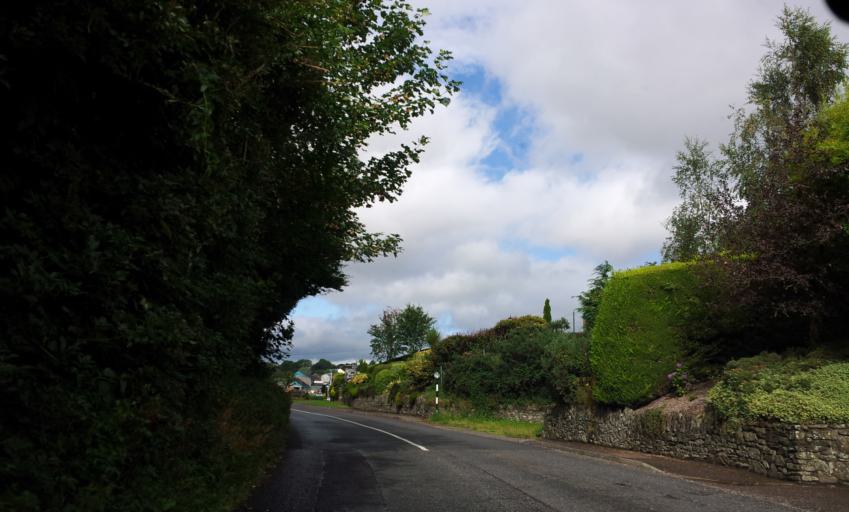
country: IE
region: Munster
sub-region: County Cork
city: Blarney
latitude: 51.9322
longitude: -8.5566
